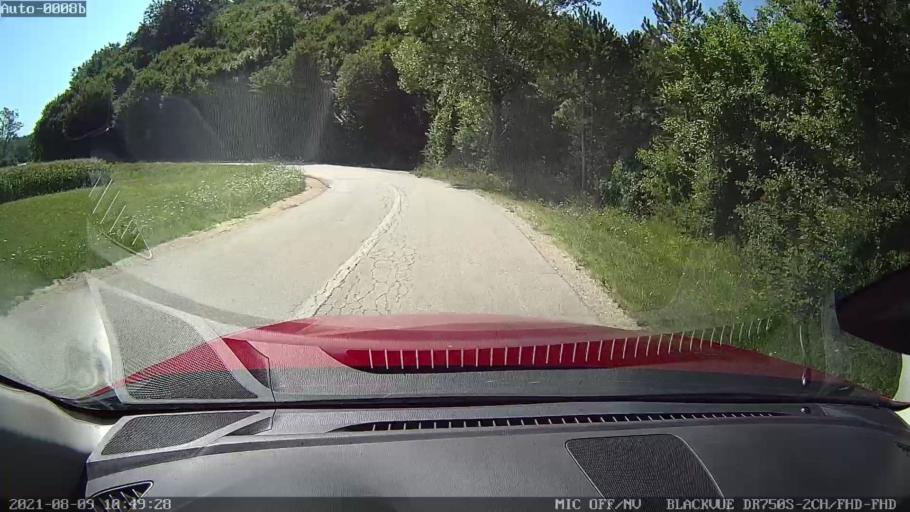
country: HR
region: Istarska
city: Pazin
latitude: 45.2669
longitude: 14.0317
